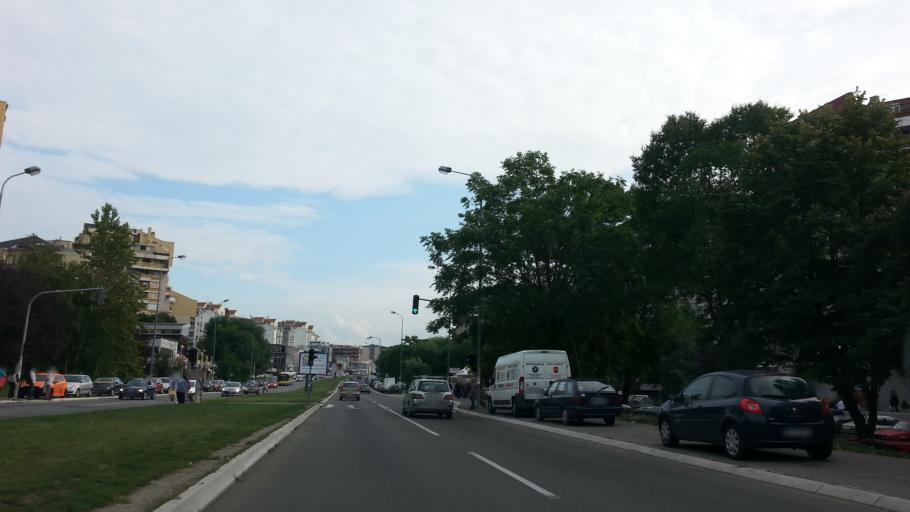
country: RS
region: Central Serbia
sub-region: Belgrade
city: Cukarica
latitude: 44.7633
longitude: 20.4138
